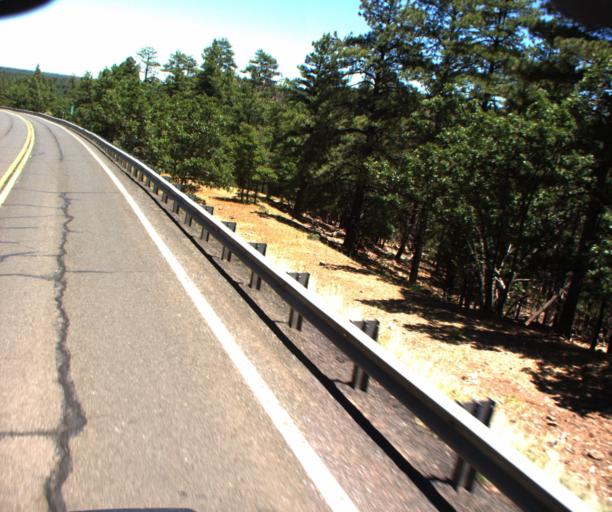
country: US
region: Arizona
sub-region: Gila County
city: Pine
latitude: 34.5957
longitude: -111.2445
